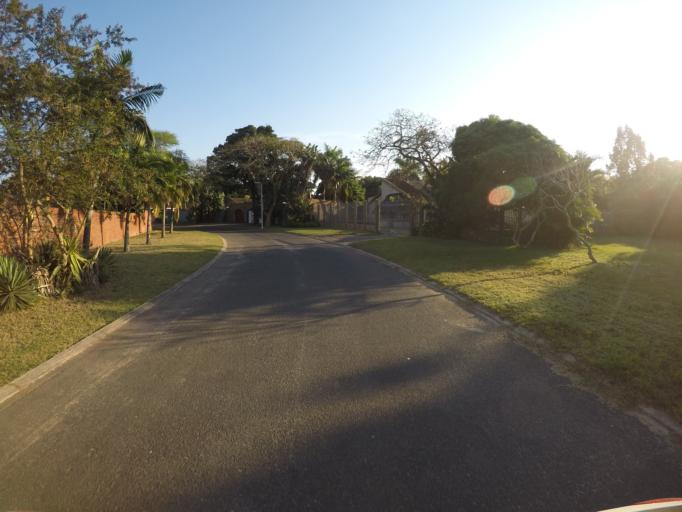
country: ZA
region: KwaZulu-Natal
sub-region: uThungulu District Municipality
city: Richards Bay
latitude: -28.7793
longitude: 32.1144
